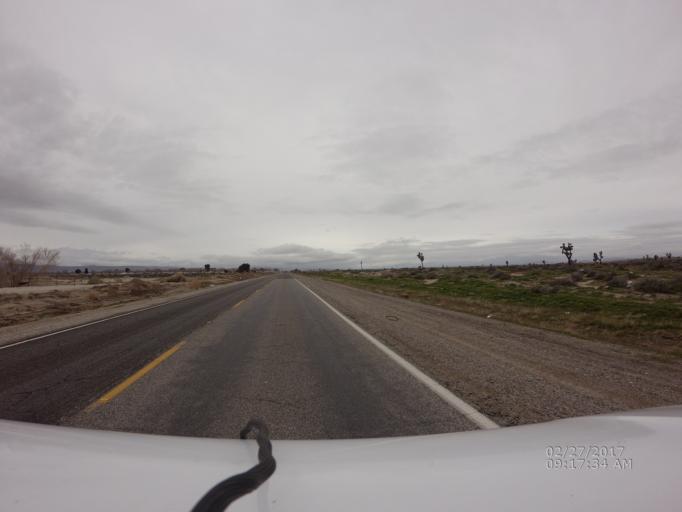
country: US
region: California
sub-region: Los Angeles County
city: Lancaster
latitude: 34.7189
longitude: -118.1029
